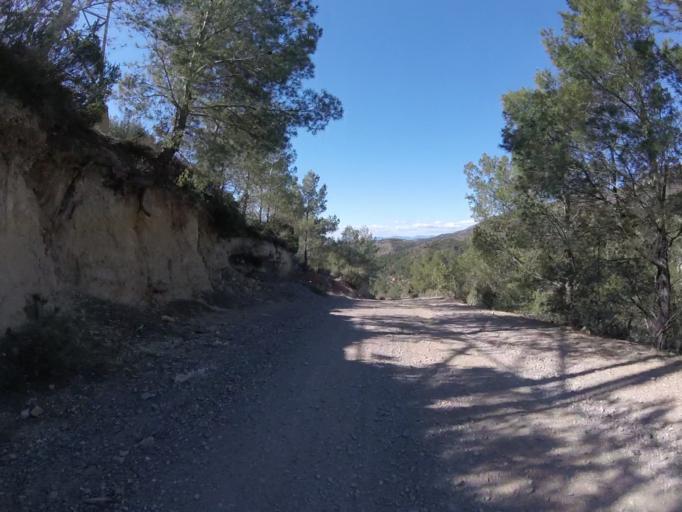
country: ES
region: Valencia
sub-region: Provincia de Castello
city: Benicassim
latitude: 40.0762
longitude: 0.0769
